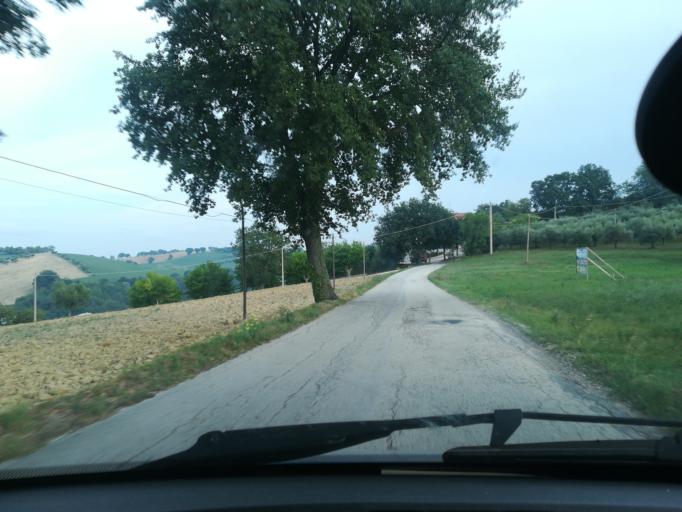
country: IT
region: The Marches
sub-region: Provincia di Macerata
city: Macerata
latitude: 43.3074
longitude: 13.4763
